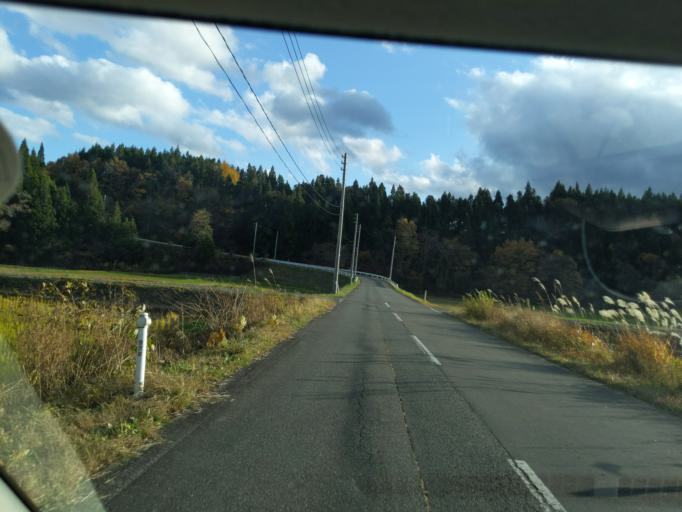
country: JP
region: Iwate
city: Mizusawa
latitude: 39.1225
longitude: 140.9743
